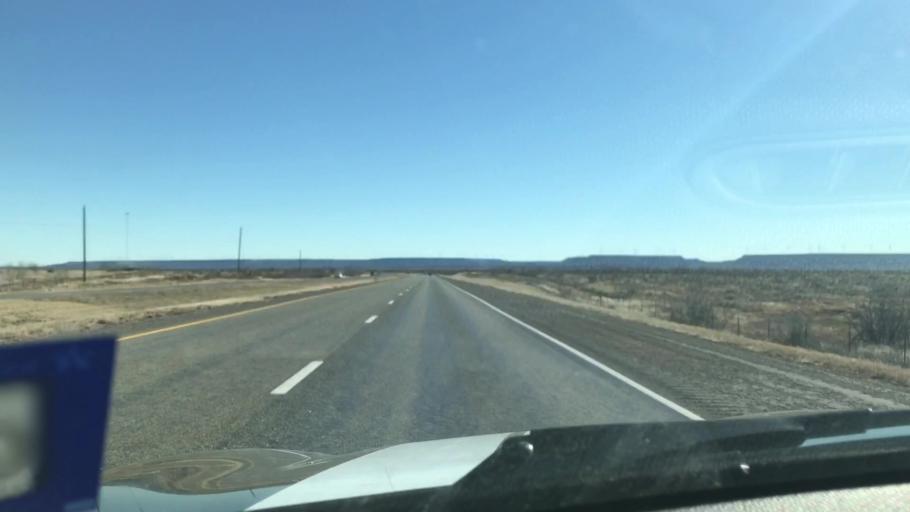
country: US
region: Texas
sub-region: Garza County
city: Post
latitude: 33.0796
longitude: -101.2396
